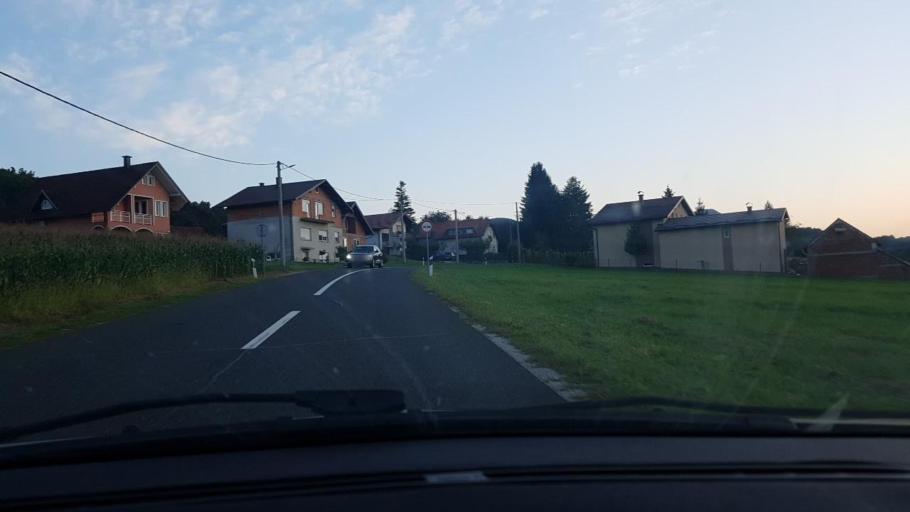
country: HR
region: Varazdinska
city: Lepoglava
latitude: 46.2240
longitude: 15.9773
